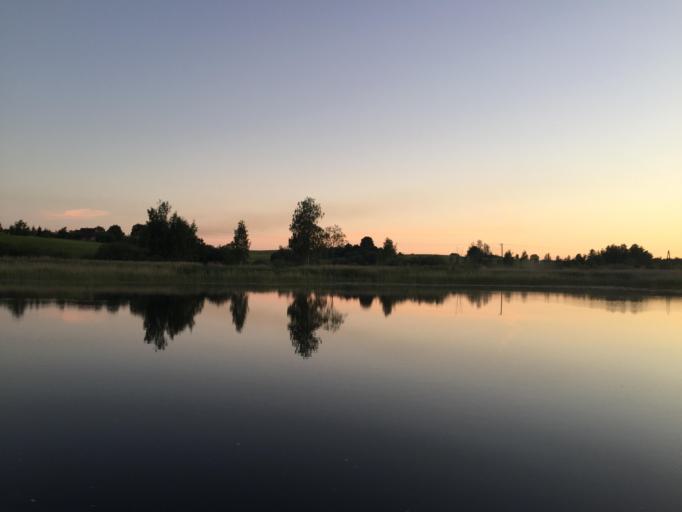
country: LV
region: Rezekne
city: Rezekne
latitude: 56.3666
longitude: 27.4128
